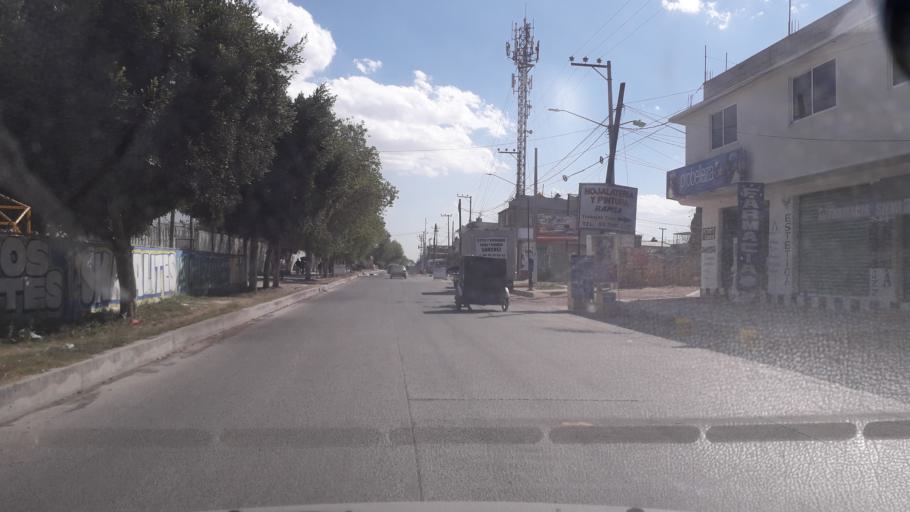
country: MX
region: Mexico
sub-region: Jaltenco
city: Alborada Jaltenco
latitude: 19.6563
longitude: -99.0681
